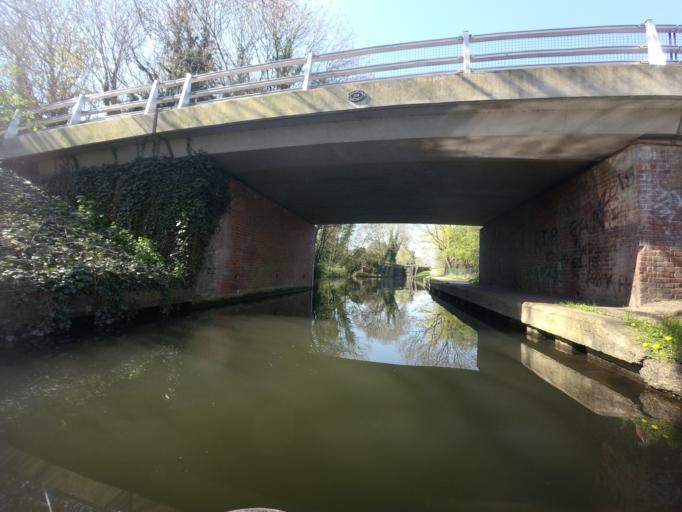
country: GB
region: England
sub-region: Hertfordshire
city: Kings Langley
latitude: 51.7133
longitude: -0.4438
